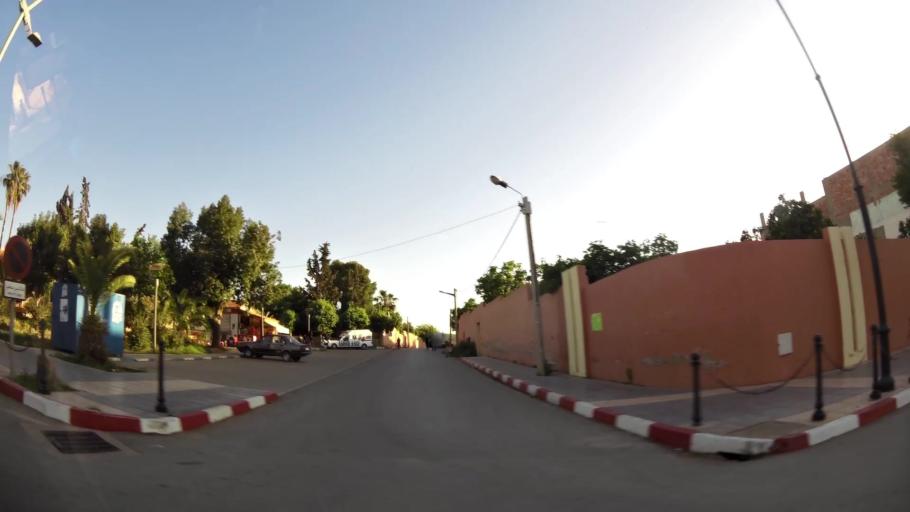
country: MA
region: Oriental
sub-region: Berkane-Taourirt
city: Berkane
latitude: 34.9260
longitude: -2.3258
